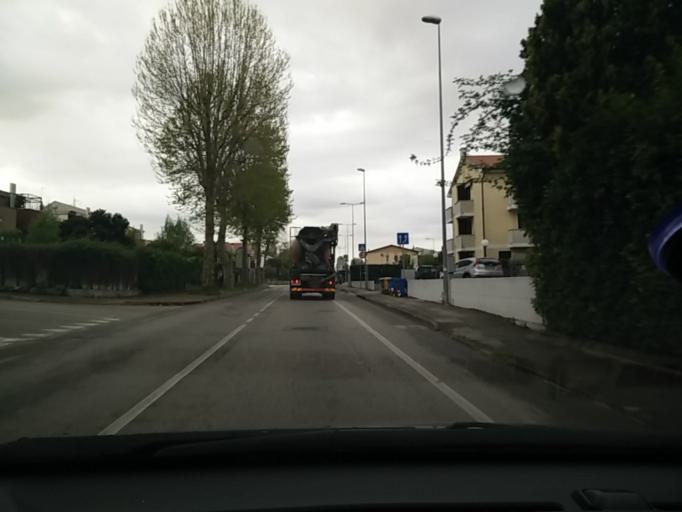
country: IT
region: Veneto
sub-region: Provincia di Treviso
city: Silea
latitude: 45.6527
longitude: 12.3027
